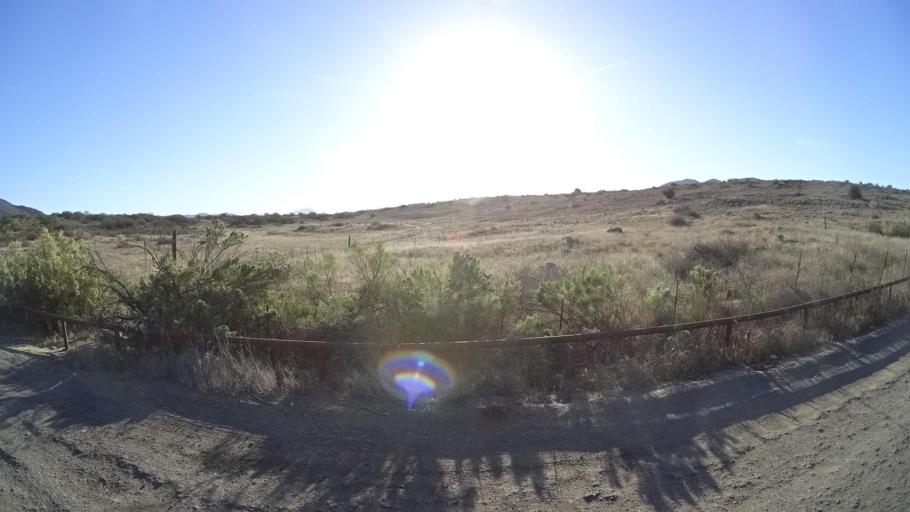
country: US
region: California
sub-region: San Diego County
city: Jamul
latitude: 32.6996
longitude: -116.9049
